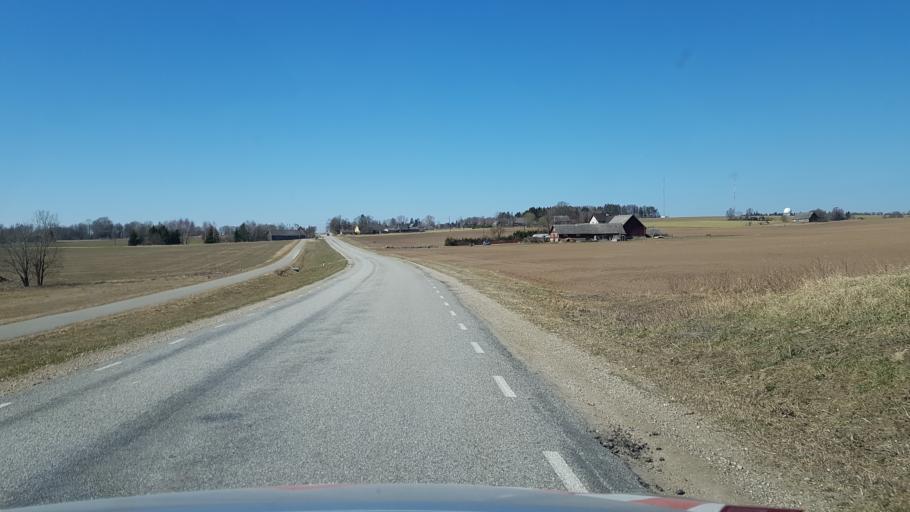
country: EE
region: Laeaene-Virumaa
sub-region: Vinni vald
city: Vinni
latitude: 59.0686
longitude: 26.5454
